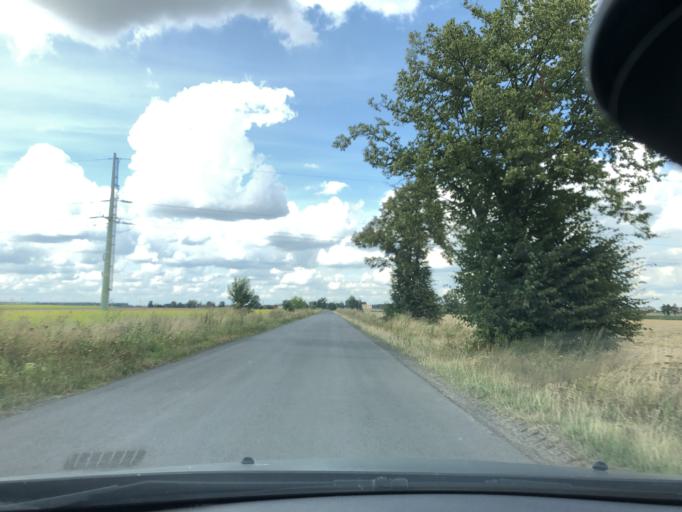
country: PL
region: Lodz Voivodeship
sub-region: Powiat wieruszowski
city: Walichnowy
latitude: 51.2395
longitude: 18.3881
